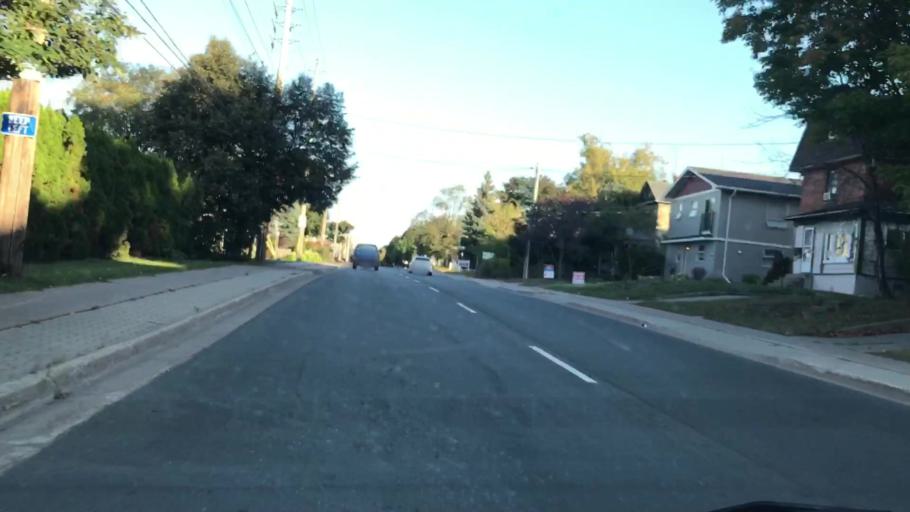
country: CA
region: Ontario
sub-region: Algoma
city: Sault Ste. Marie
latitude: 46.5104
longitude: -84.3266
